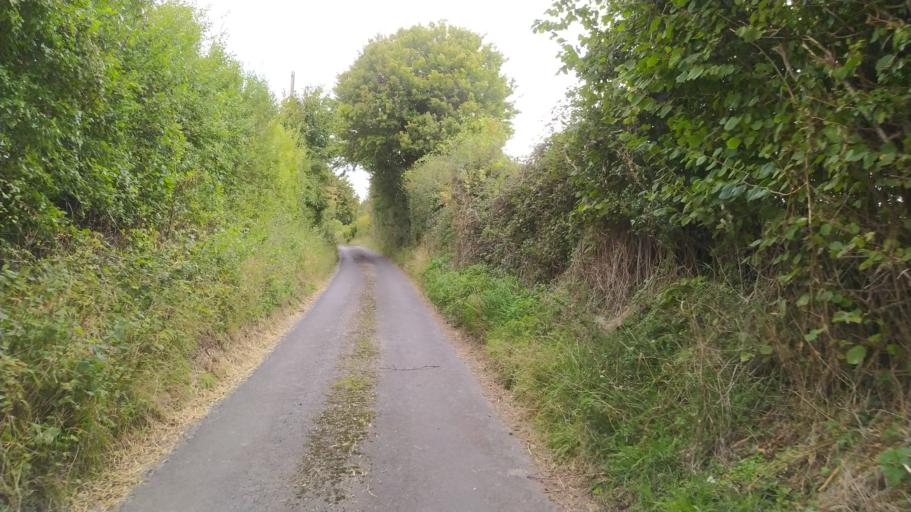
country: GB
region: England
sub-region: Hampshire
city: Long Sutton
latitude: 51.1812
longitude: -0.9019
